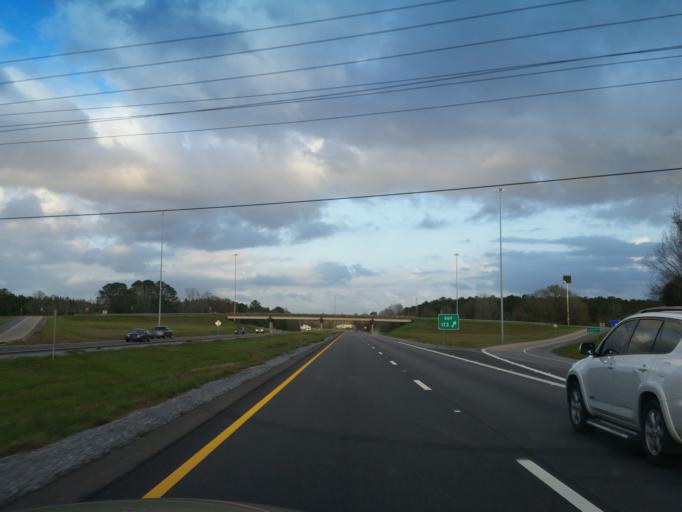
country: US
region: Mississippi
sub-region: Jones County
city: Sharon
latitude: 31.9058
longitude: -89.0180
